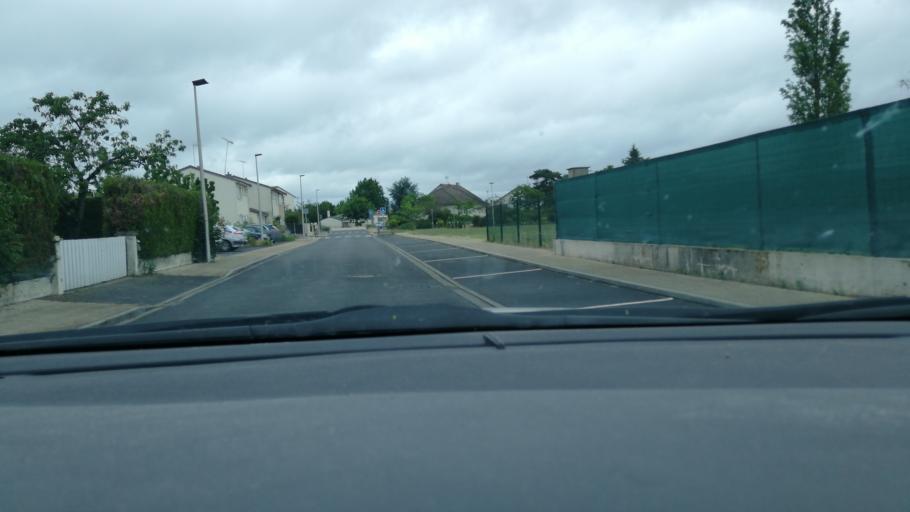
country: FR
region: Poitou-Charentes
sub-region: Departement de la Vienne
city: Antran
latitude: 46.8785
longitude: 0.5693
